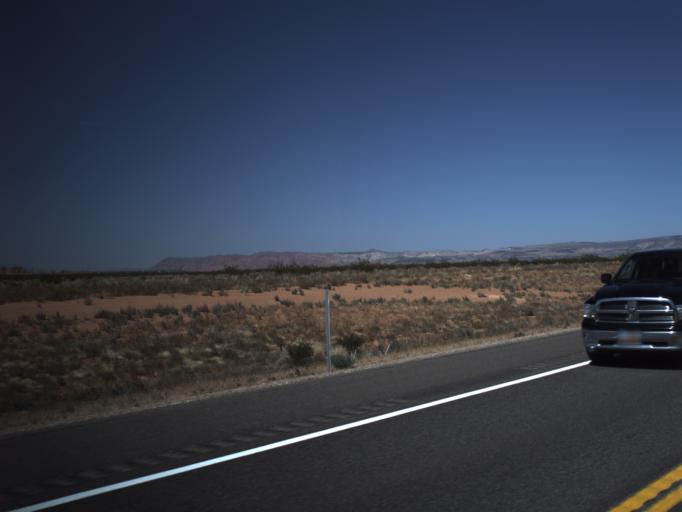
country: US
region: Utah
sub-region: Washington County
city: Washington
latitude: 37.0282
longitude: -113.4852
